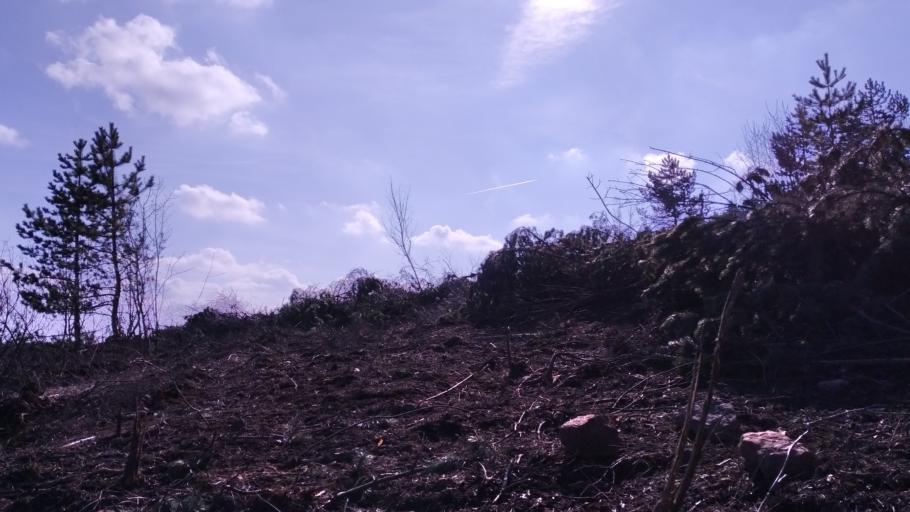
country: HU
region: Pest
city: Urom
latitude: 47.6209
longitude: 19.0147
